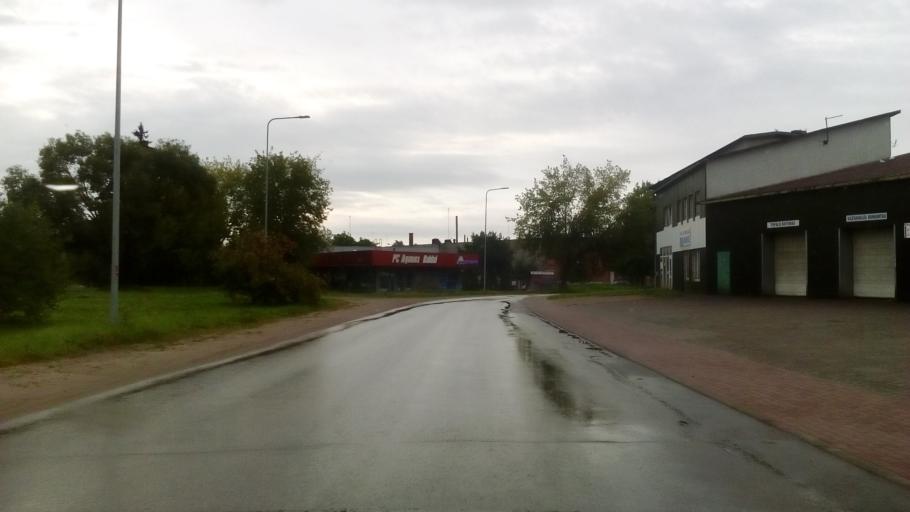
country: LT
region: Alytaus apskritis
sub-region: Alytus
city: Alytus
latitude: 54.3896
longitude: 24.0392
